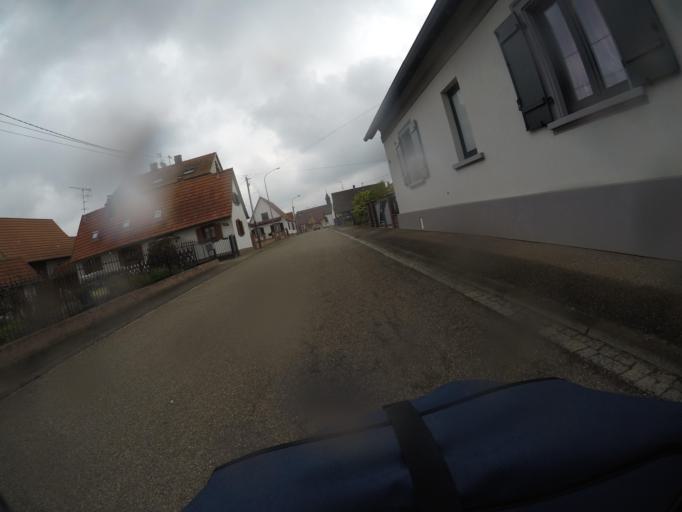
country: FR
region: Alsace
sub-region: Departement du Bas-Rhin
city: Roppenheim
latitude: 48.8235
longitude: 8.0840
